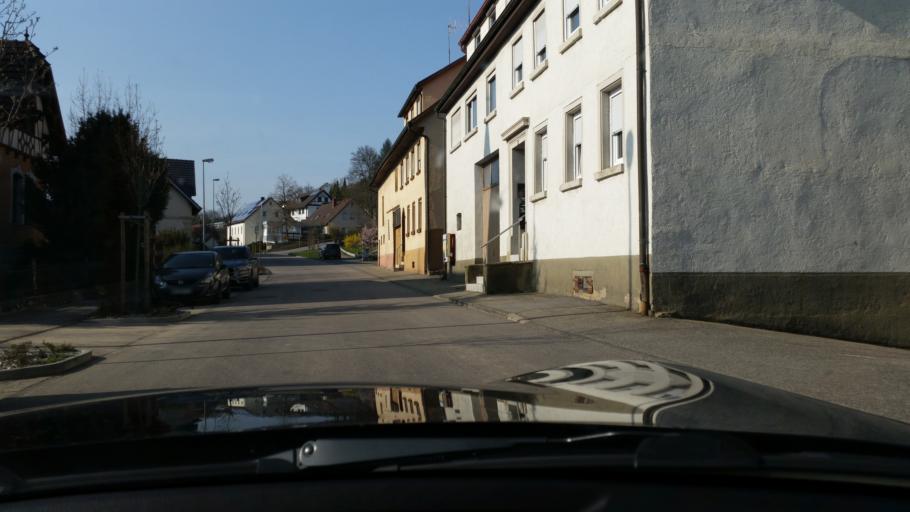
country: DE
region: Baden-Wuerttemberg
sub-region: Regierungsbezirk Stuttgart
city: Mockmuhl
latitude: 49.3257
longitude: 9.3587
